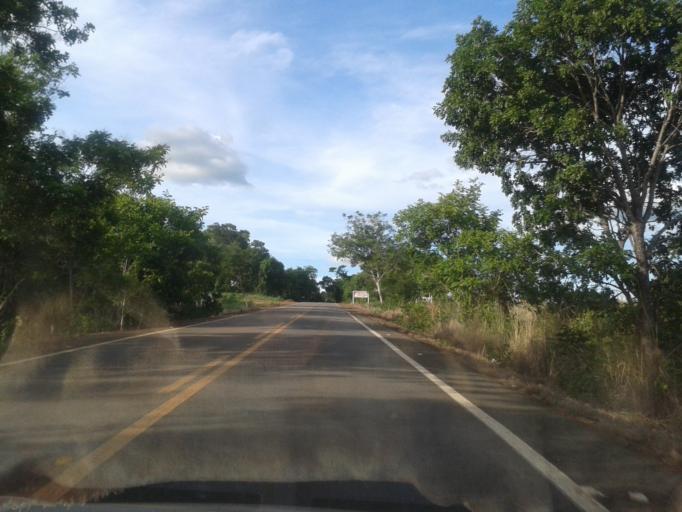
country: BR
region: Goias
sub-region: Crixas
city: Crixas
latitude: -13.9791
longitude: -50.3223
